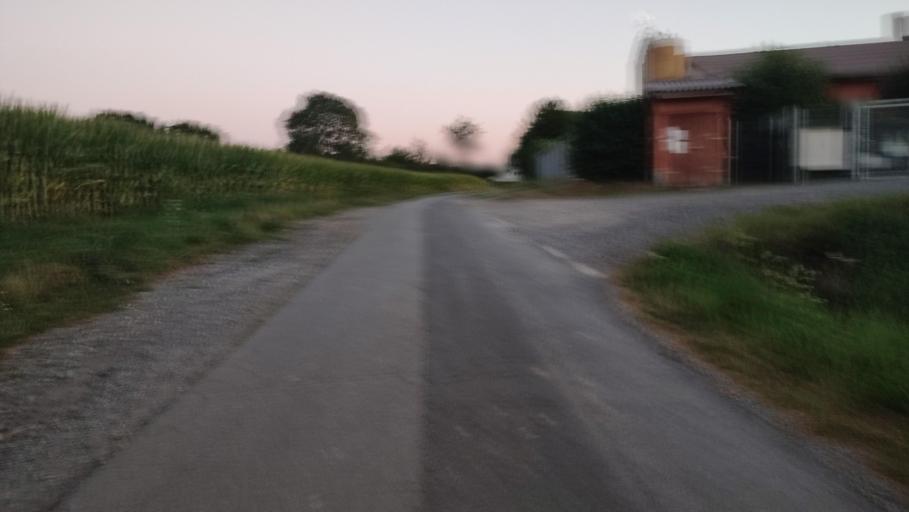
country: DE
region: North Rhine-Westphalia
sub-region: Regierungsbezirk Arnsberg
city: Unna
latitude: 51.5244
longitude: 7.7268
